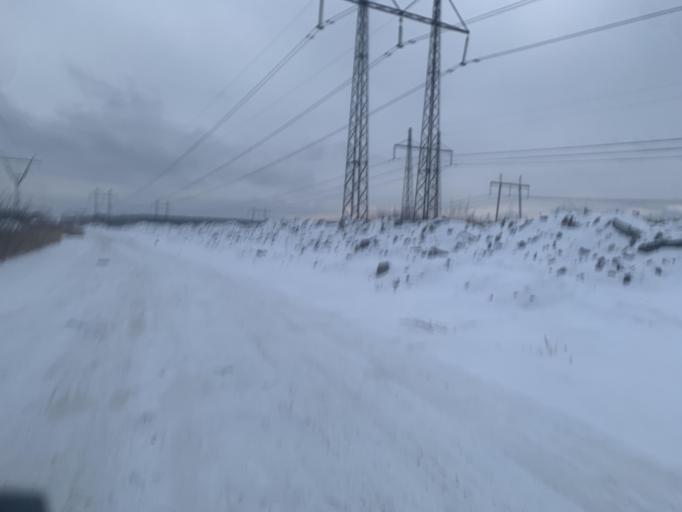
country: RU
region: Chelyabinsk
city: Roshchino
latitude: 55.1863
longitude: 61.2576
